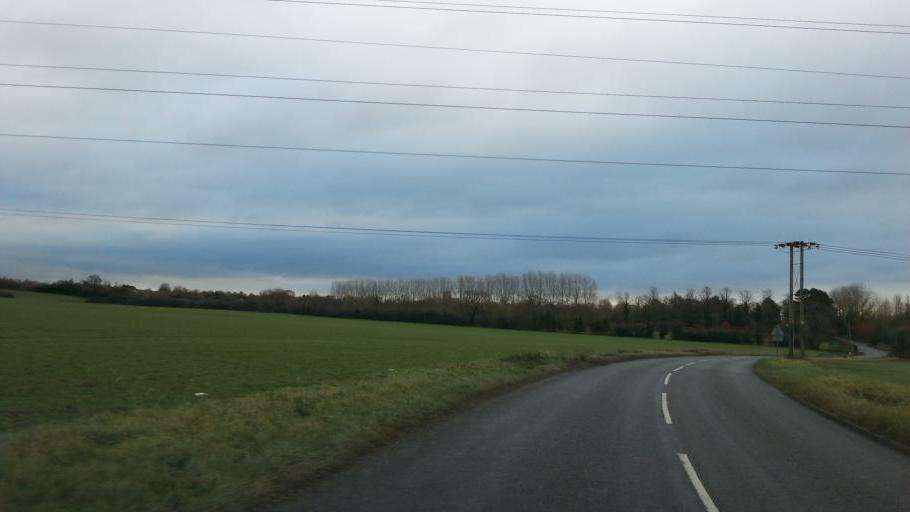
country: GB
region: England
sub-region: Suffolk
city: Framlingham
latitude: 52.3042
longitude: 1.3536
